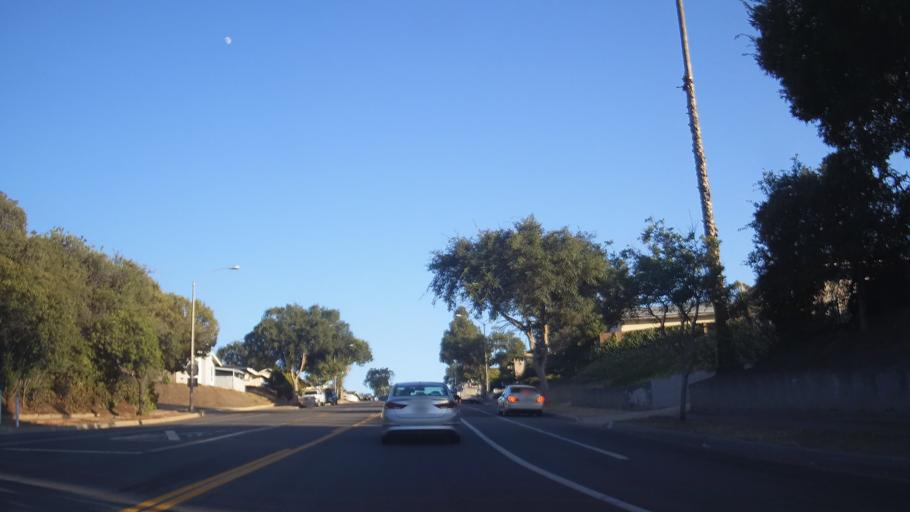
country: US
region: California
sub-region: San Diego County
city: La Mesa
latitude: 32.7850
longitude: -116.9984
